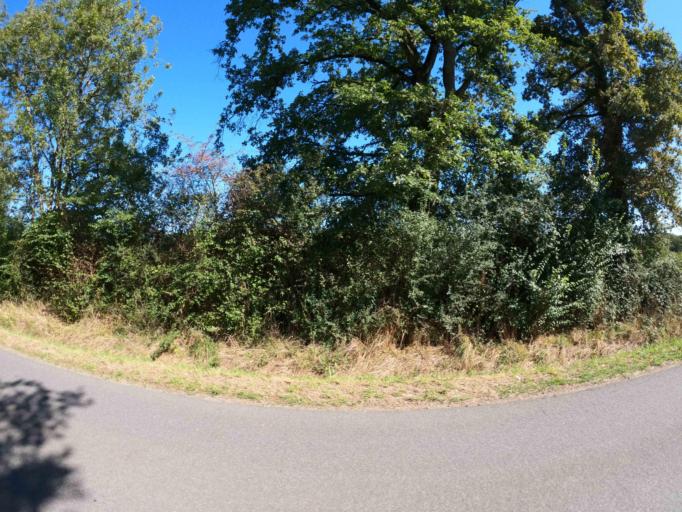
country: FR
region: Limousin
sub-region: Departement de la Haute-Vienne
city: Le Dorat
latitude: 46.2635
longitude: 1.0329
